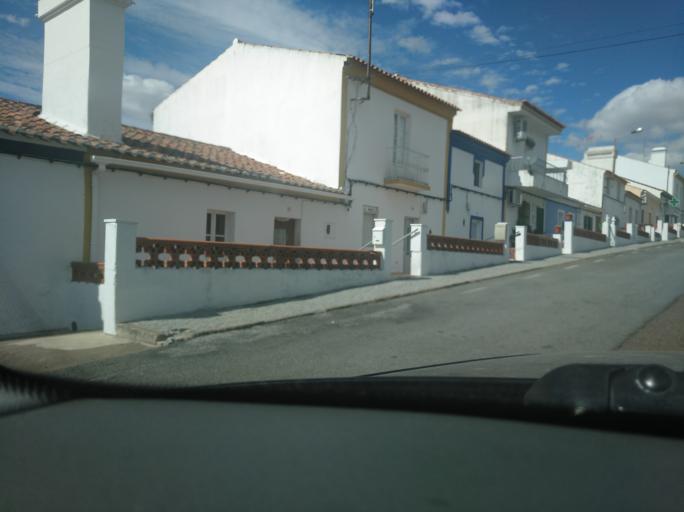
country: ES
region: Extremadura
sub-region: Provincia de Badajoz
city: La Codosera
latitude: 39.1564
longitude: -7.1936
